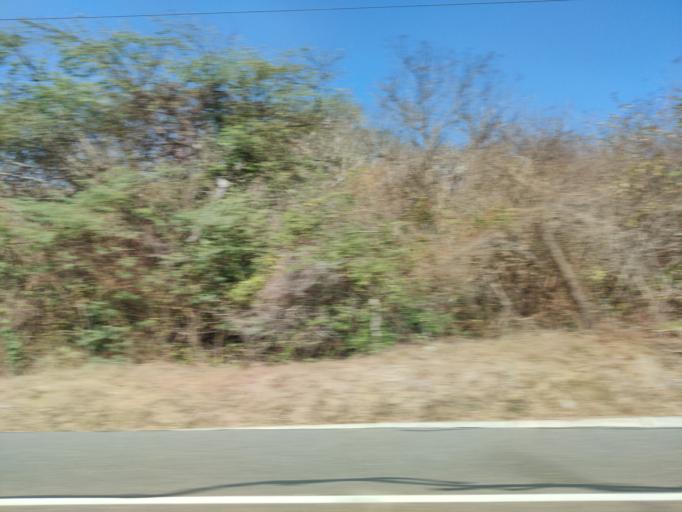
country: CO
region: Atlantico
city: Puerto Colombia
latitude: 10.9620
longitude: -75.0001
